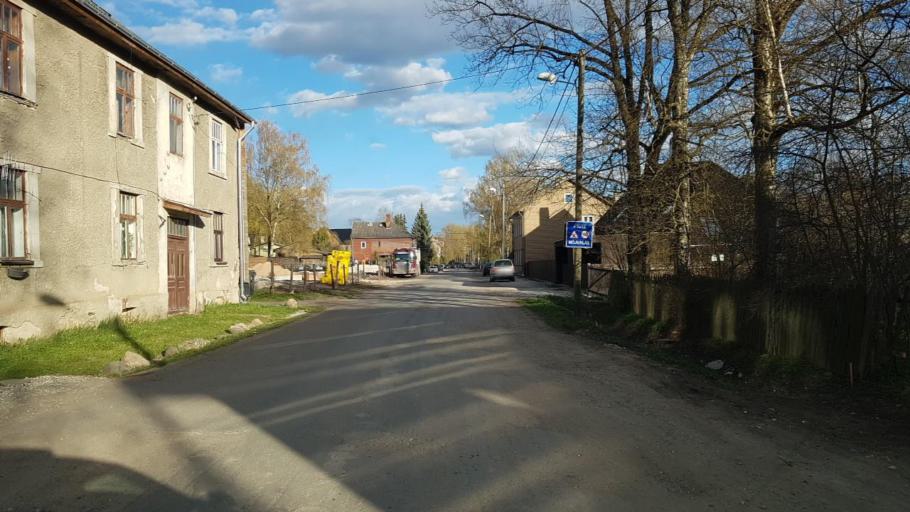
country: EE
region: Tartu
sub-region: Tartu linn
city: Tartu
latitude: 58.3916
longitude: 26.7163
